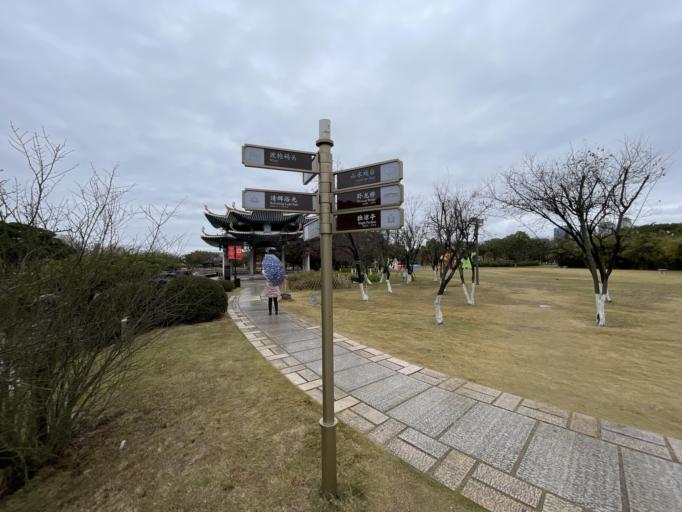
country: CN
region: Zhejiang Sheng
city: Oubei
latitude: 28.0312
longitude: 120.6399
